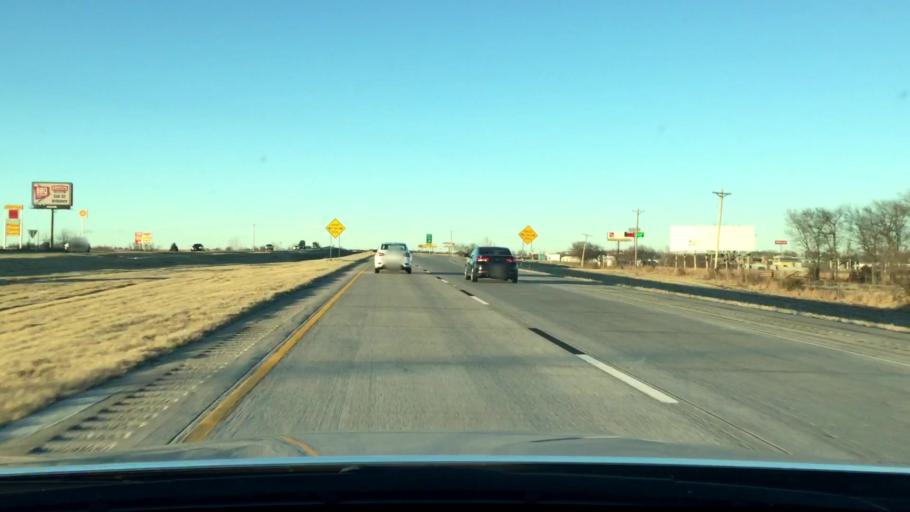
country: US
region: Oklahoma
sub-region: Love County
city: Marietta
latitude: 33.9359
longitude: -97.1348
